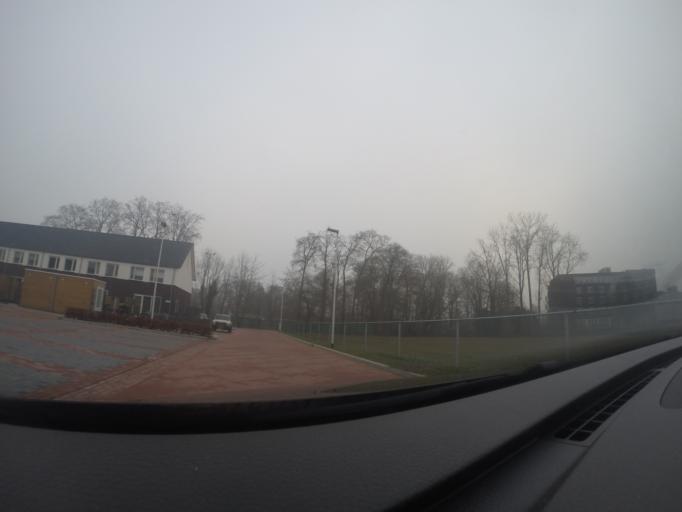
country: NL
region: Gelderland
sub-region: Gemeente Zutphen
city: Zutphen
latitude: 52.1472
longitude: 6.2074
